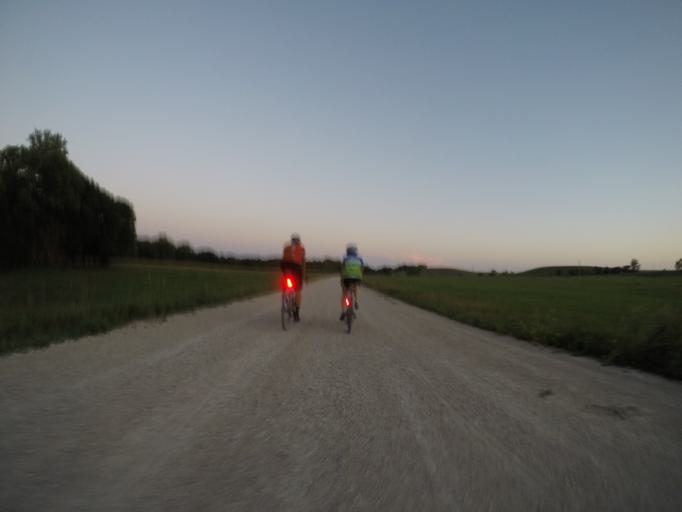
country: US
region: Kansas
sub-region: Riley County
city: Ogden
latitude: 38.9745
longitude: -96.5627
